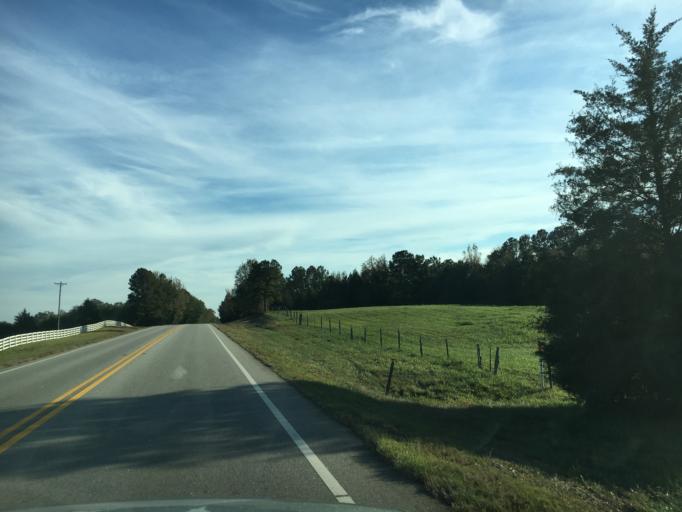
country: US
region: Georgia
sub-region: Wilkes County
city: Washington
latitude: 33.9197
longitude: -82.7523
